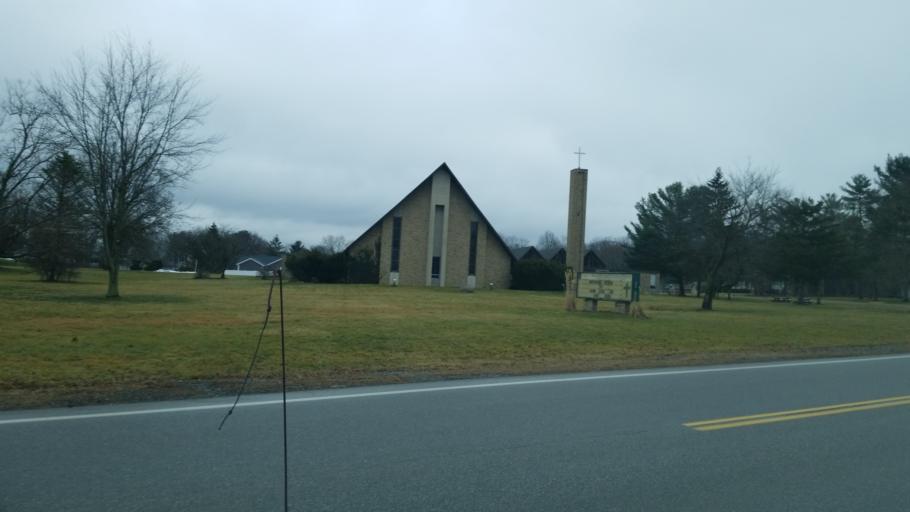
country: US
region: Ohio
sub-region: Summit County
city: Akron
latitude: 41.1245
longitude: -81.5494
